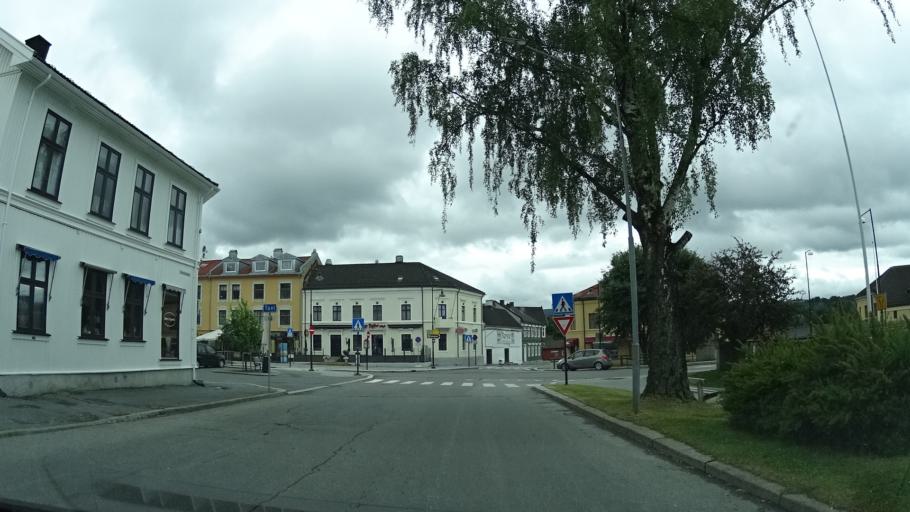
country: NO
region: Buskerud
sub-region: Ringerike
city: Honefoss
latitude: 60.1705
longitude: 10.2578
